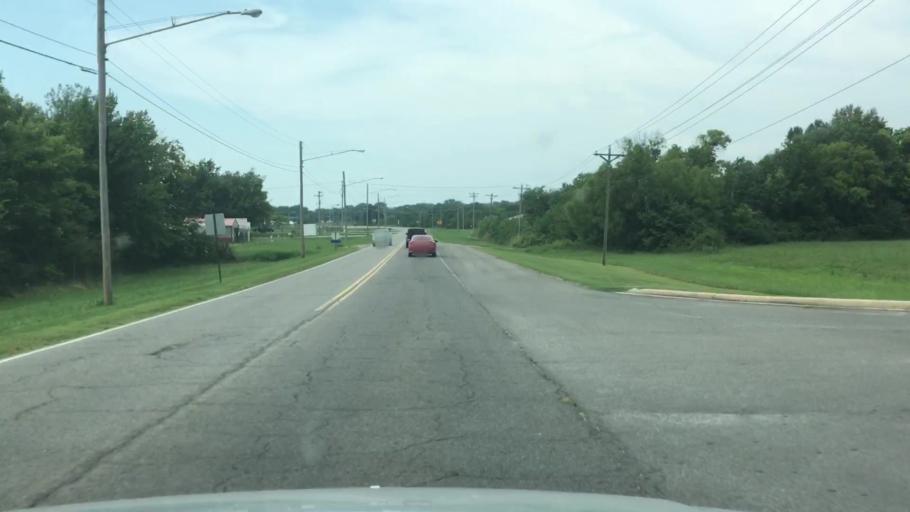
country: US
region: Oklahoma
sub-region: Cherokee County
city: Tahlequah
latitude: 35.9191
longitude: -94.9971
